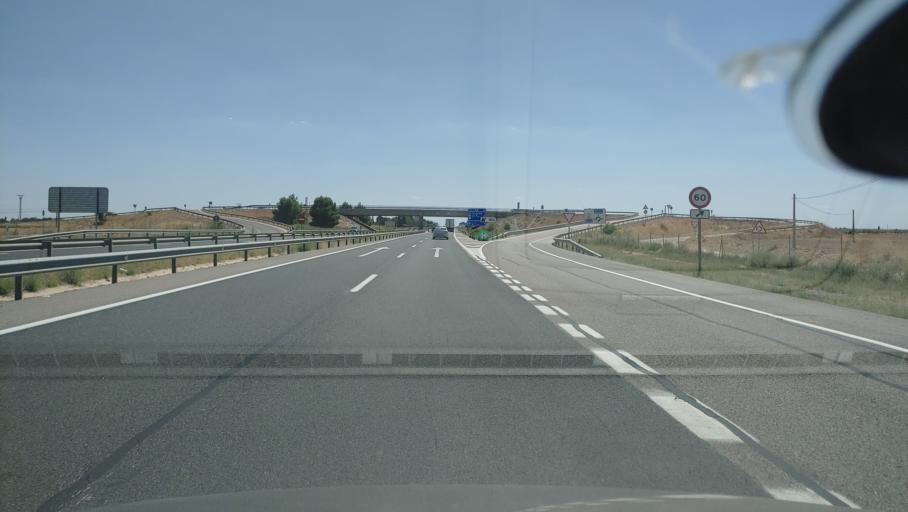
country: ES
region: Castille-La Mancha
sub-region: Provincia de Ciudad Real
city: Villarta de San Juan
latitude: 39.1250
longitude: -3.3780
